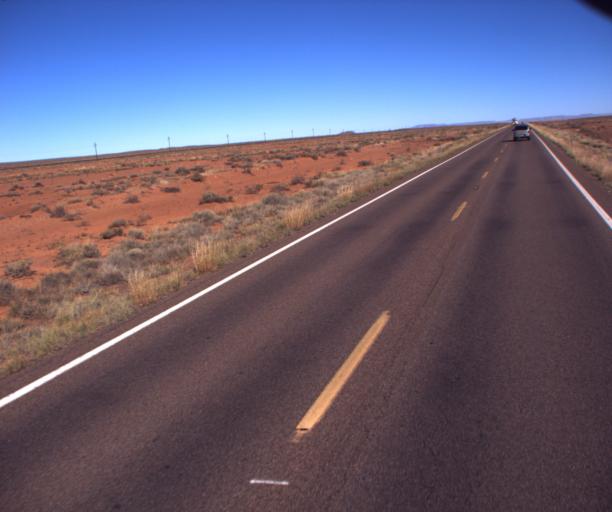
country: US
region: Arizona
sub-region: Navajo County
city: Holbrook
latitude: 34.8021
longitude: -110.1358
